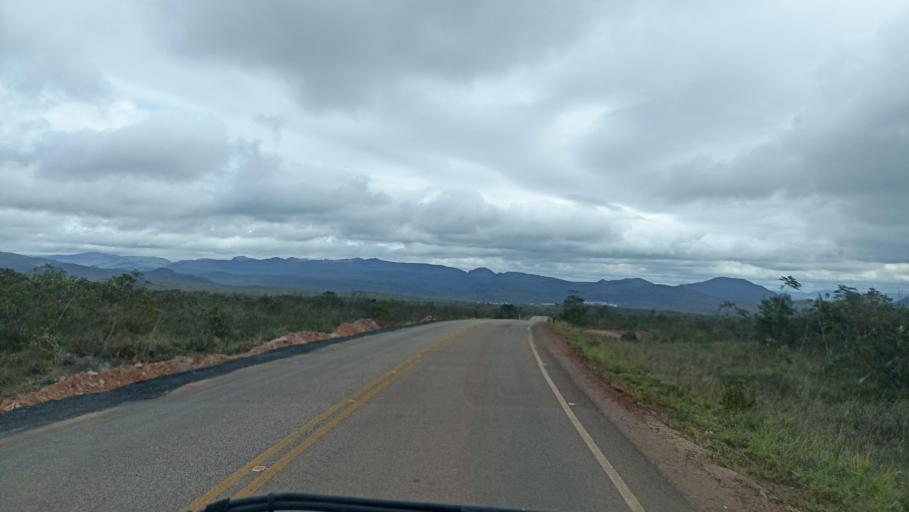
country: BR
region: Bahia
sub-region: Andarai
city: Vera Cruz
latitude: -12.9617
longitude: -41.3215
